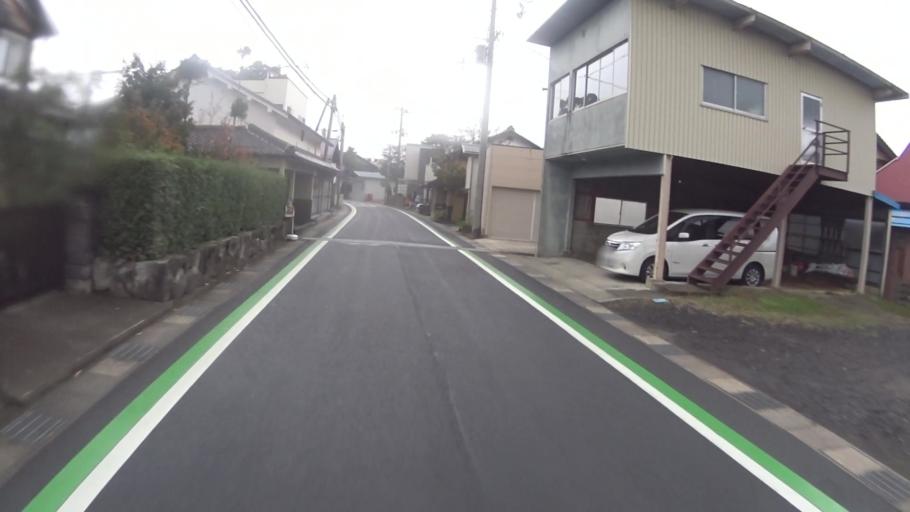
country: JP
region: Kyoto
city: Miyazu
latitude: 35.5445
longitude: 135.2366
